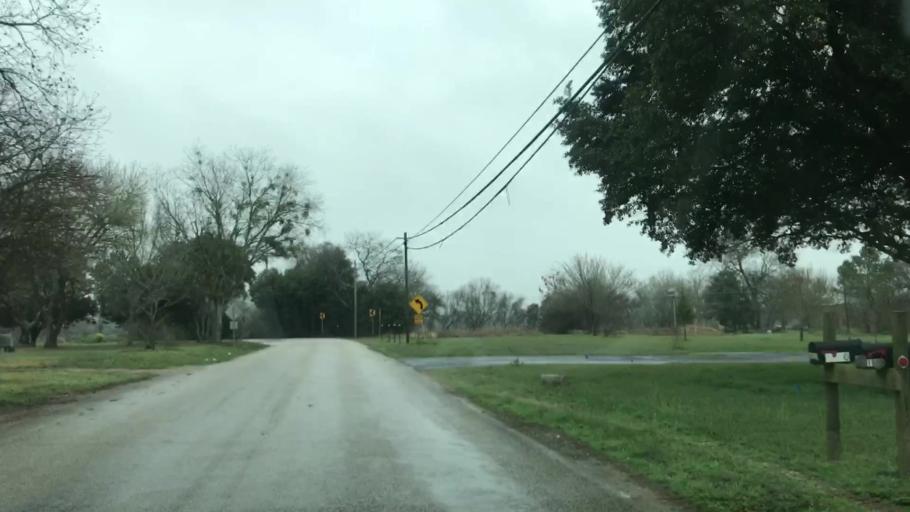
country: US
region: Texas
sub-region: Hays County
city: San Marcos
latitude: 29.8949
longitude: -97.8988
